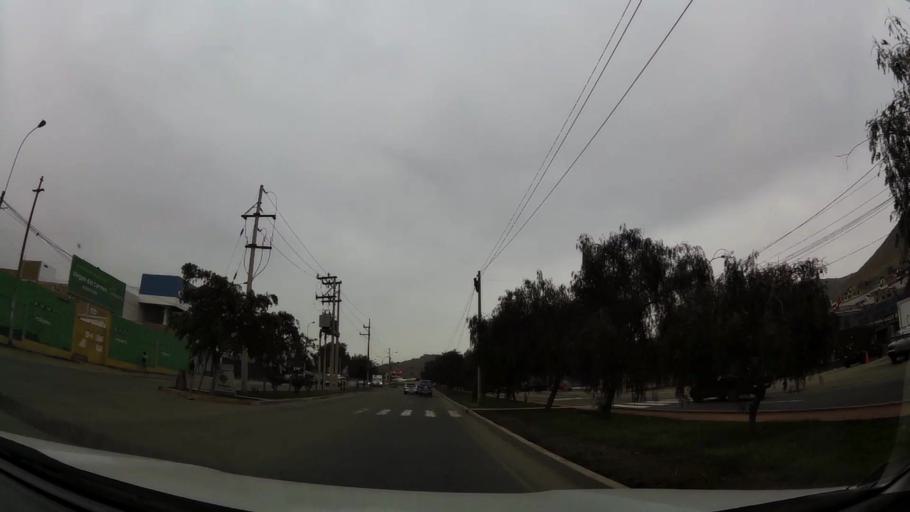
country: PE
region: Lima
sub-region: Lima
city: La Molina
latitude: -12.0863
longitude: -76.8921
